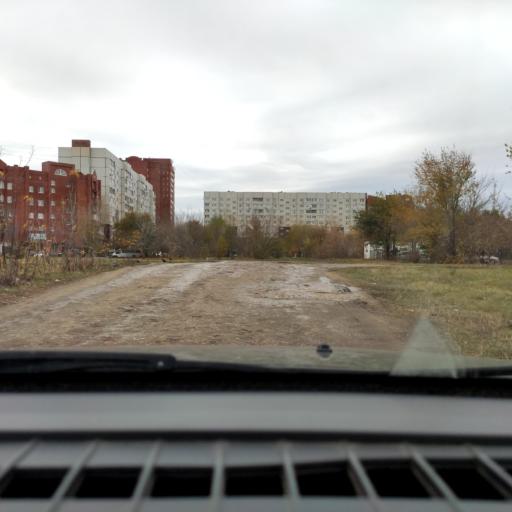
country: RU
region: Samara
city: Tol'yatti
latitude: 53.5484
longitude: 49.3218
